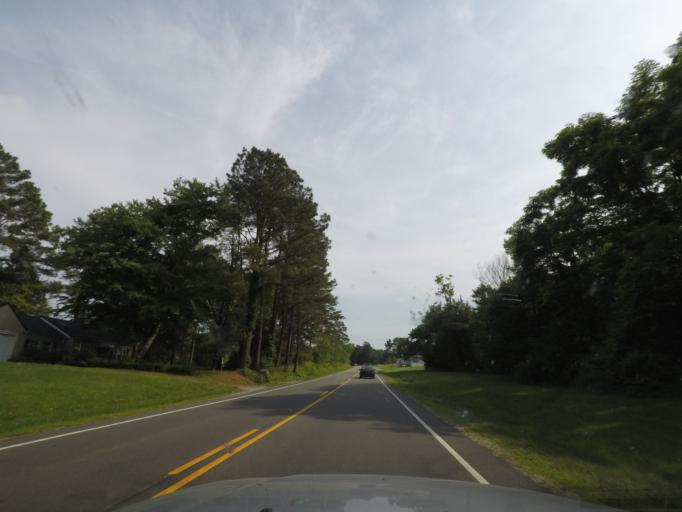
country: US
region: Virginia
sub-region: Prince Edward County
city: Hampden Sydney
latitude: 37.2372
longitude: -78.4440
